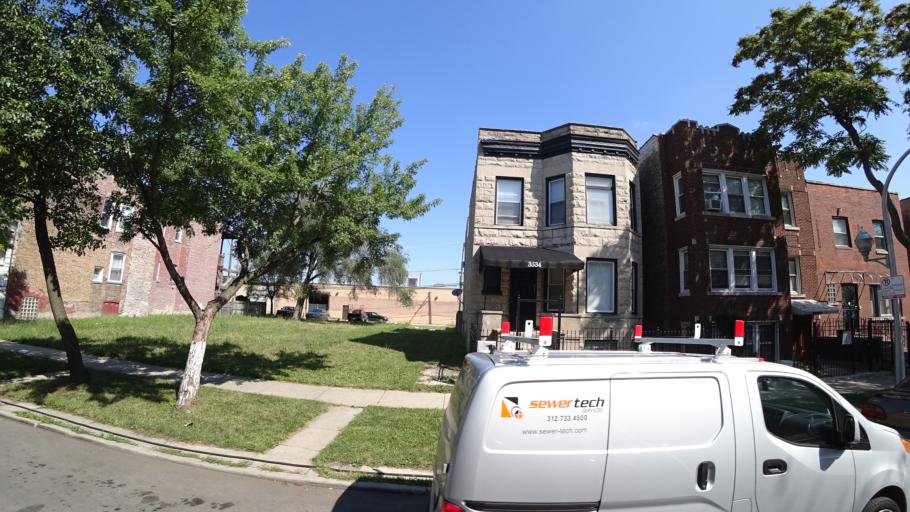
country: US
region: Illinois
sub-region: Cook County
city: Cicero
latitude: 41.8727
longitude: -87.7146
